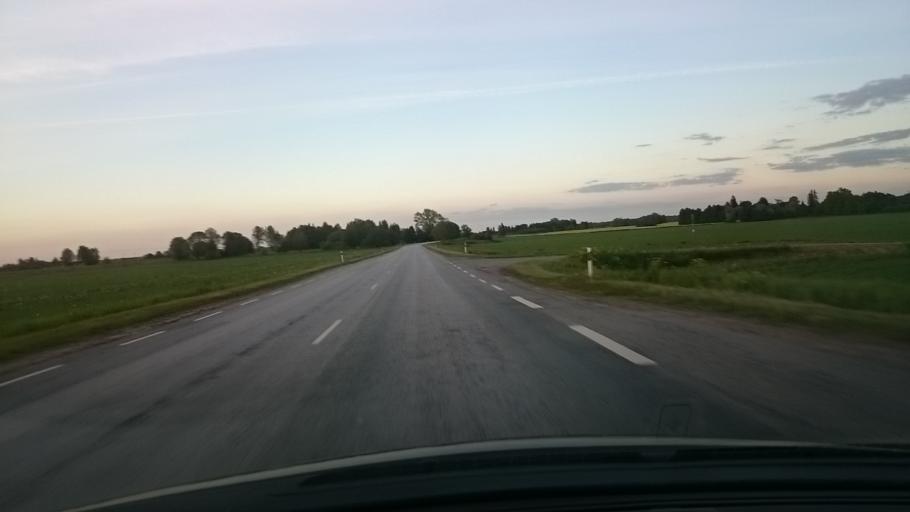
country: EE
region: Viljandimaa
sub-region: Vohma linn
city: Vohma
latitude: 58.6495
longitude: 25.5867
